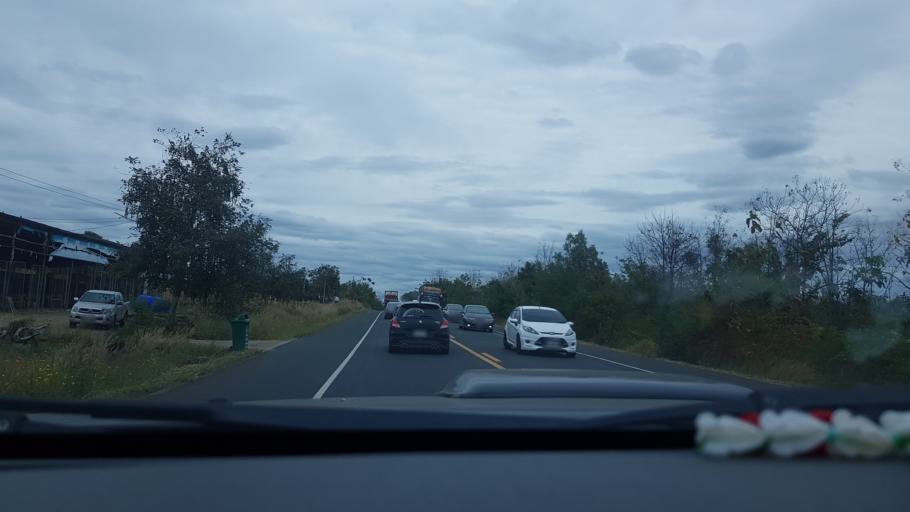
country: TH
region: Phetchabun
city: Phetchabun
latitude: 16.4717
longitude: 101.1283
